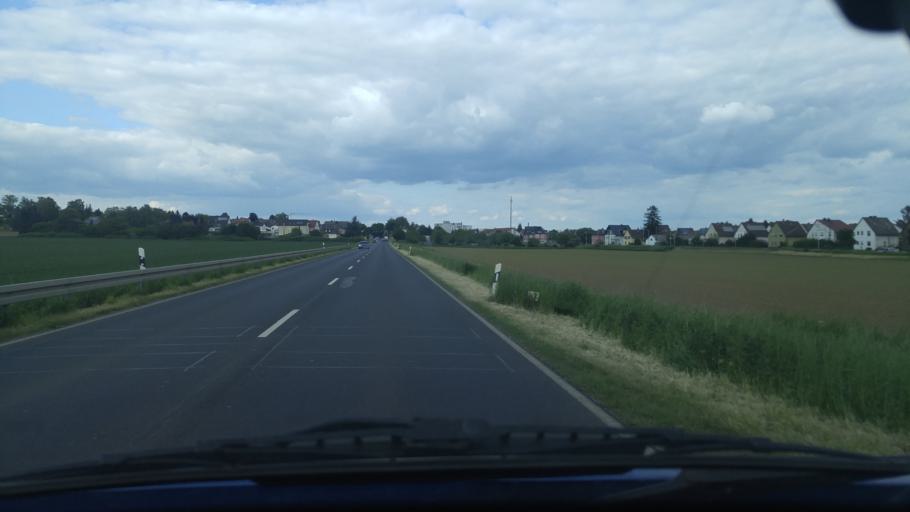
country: DE
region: Hesse
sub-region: Regierungsbezirk Darmstadt
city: Karben
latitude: 50.2498
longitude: 8.7499
